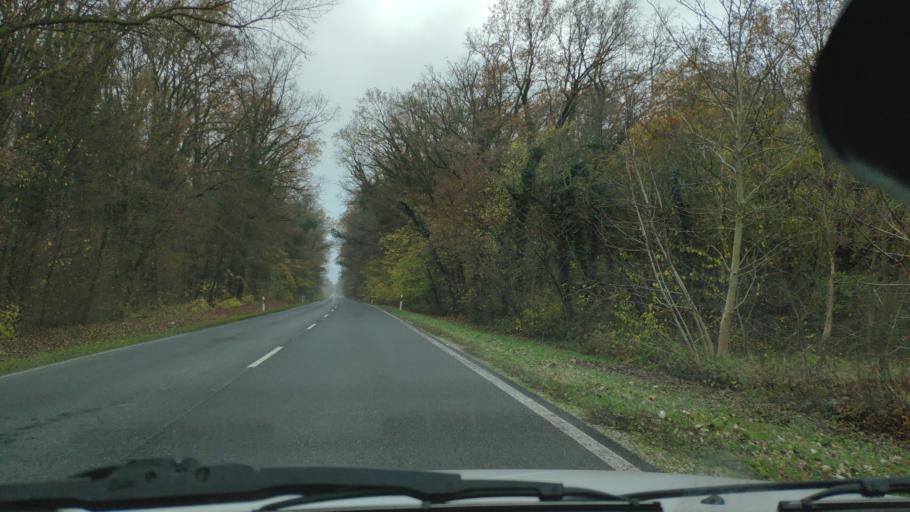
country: HU
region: Somogy
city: Balatonbereny
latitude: 46.6342
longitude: 17.2922
